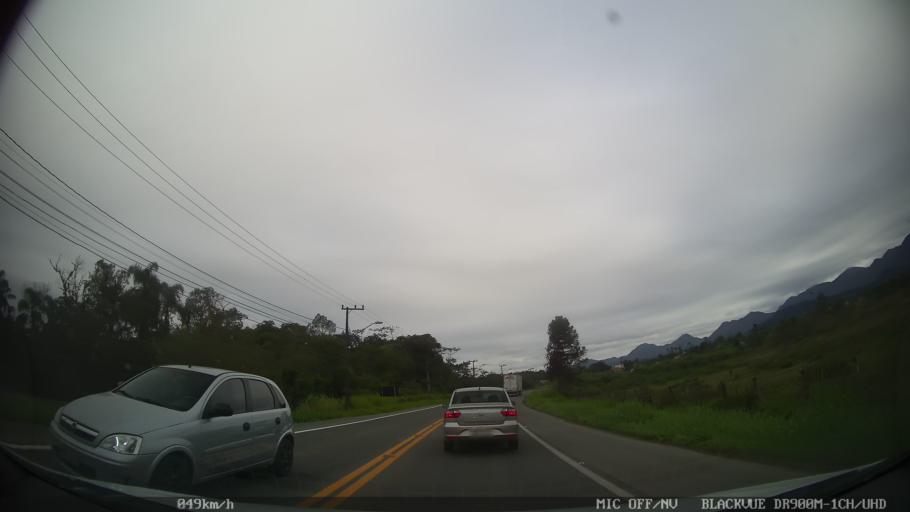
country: BR
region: Santa Catarina
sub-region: Joinville
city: Joinville
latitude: -26.3080
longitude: -48.9201
